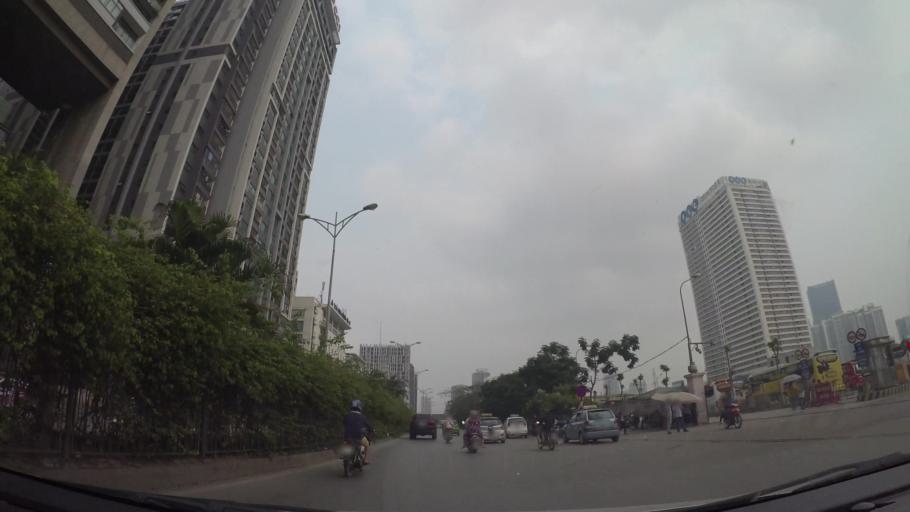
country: VN
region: Ha Noi
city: Cau Dien
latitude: 21.0292
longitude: 105.7767
